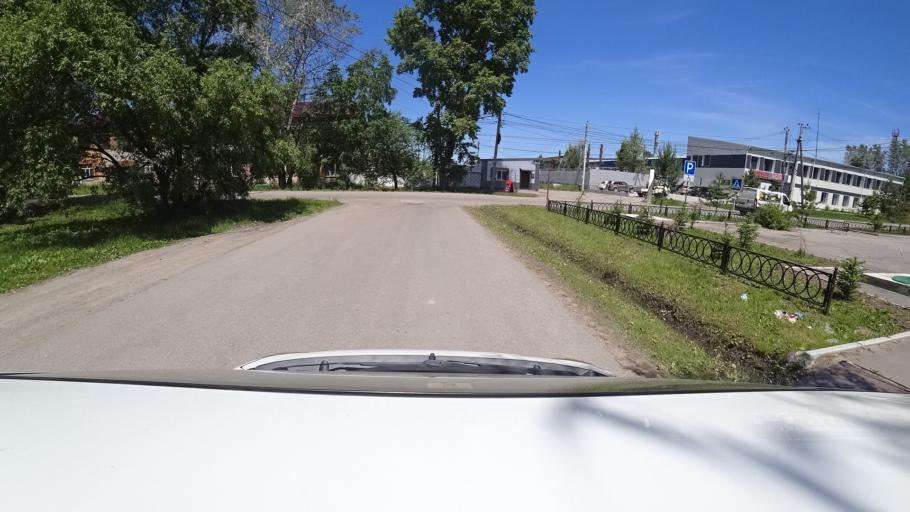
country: RU
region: Khabarovsk Krai
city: Topolevo
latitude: 48.5067
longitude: 135.1682
